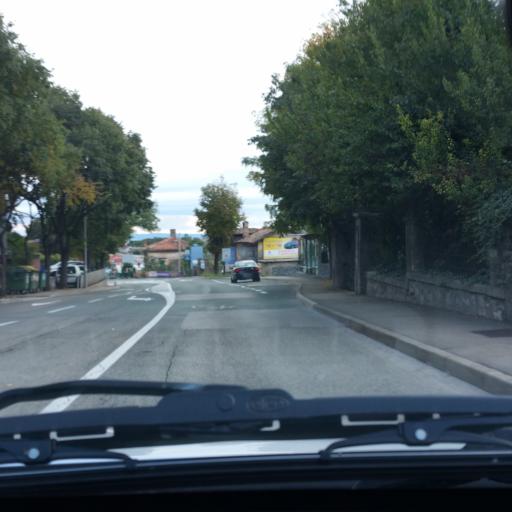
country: HR
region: Primorsko-Goranska
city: Drenova
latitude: 45.3433
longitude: 14.4239
